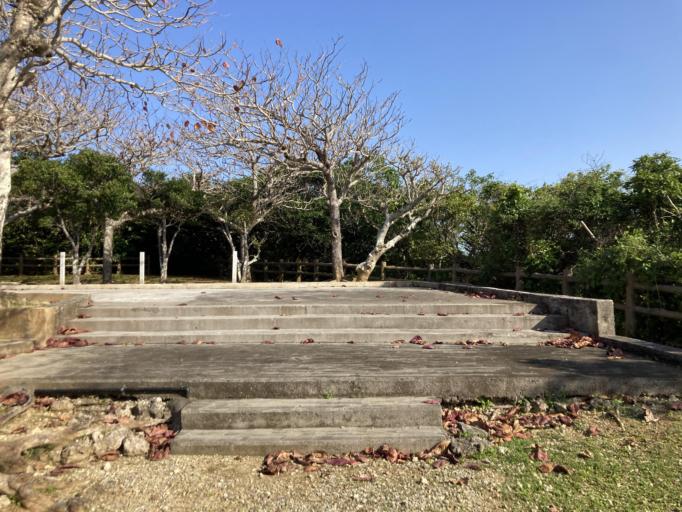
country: JP
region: Okinawa
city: Itoman
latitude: 26.1216
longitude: 127.7508
